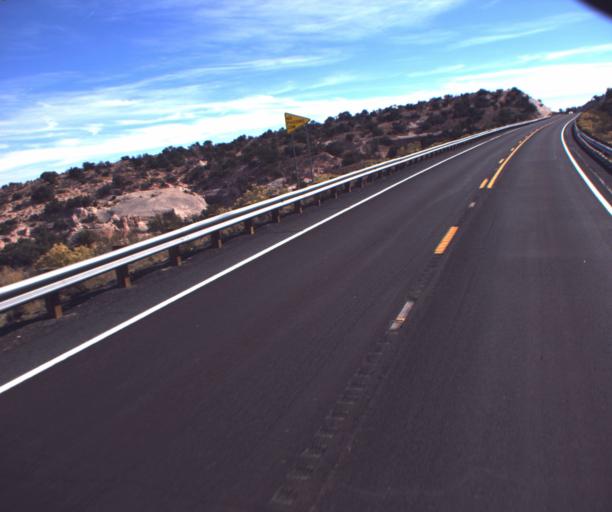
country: US
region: Arizona
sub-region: Coconino County
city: Kaibito
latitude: 36.5929
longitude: -110.8994
